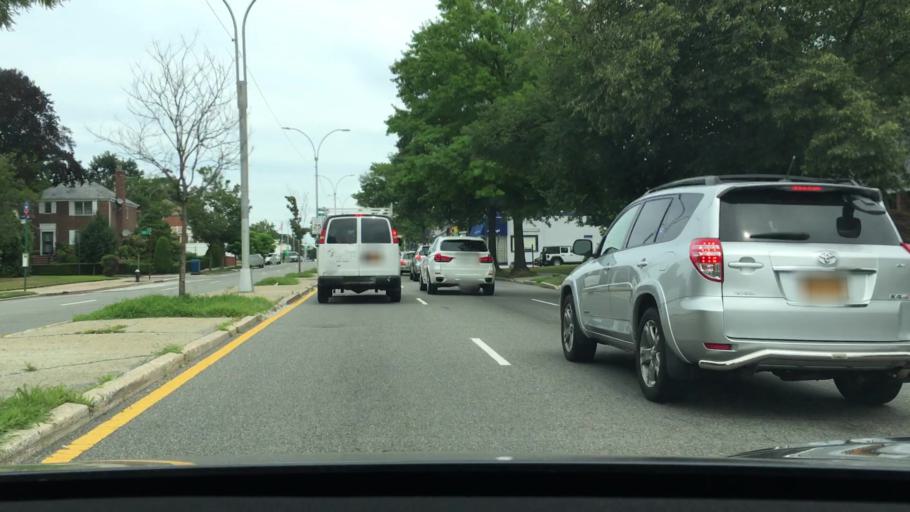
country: US
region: New York
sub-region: Nassau County
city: Bellerose Terrace
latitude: 40.7353
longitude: -73.7495
